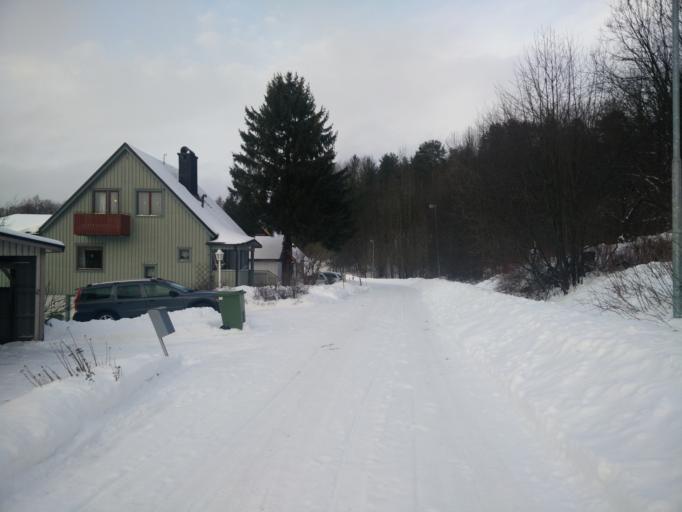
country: SE
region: Vaesternorrland
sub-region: Sundsvalls Kommun
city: Nolby
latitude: 62.2898
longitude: 17.3603
